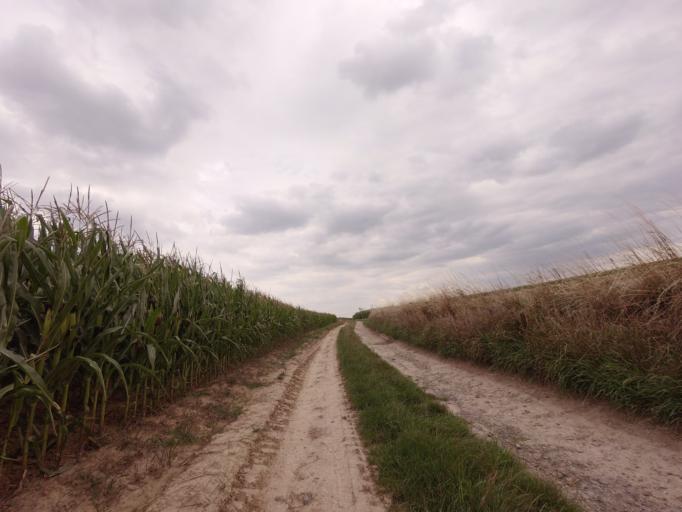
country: BE
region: Flanders
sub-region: Provincie Vlaams-Brabant
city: Grimbergen
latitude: 50.9254
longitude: 4.3822
